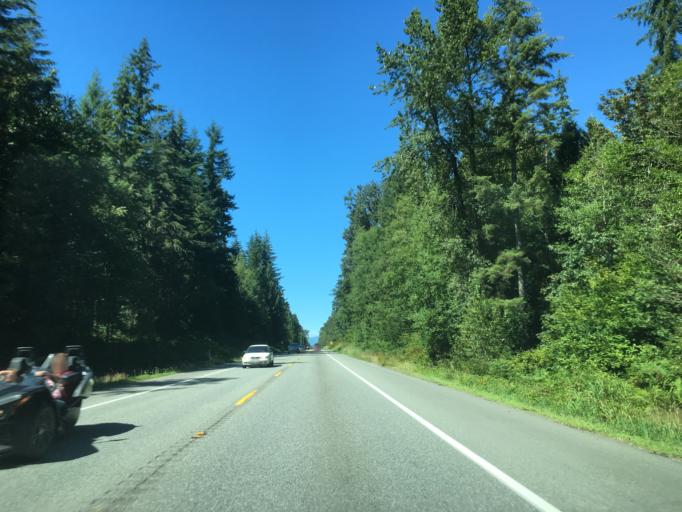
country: US
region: Washington
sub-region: Snohomish County
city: Sisco Heights
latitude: 48.1104
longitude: -122.1123
